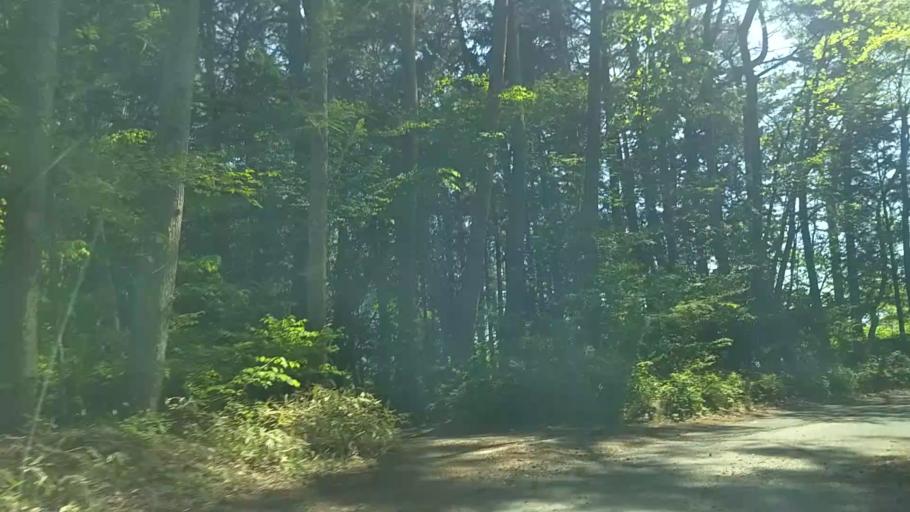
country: JP
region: Yamanashi
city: Nirasaki
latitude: 35.9056
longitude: 138.4386
